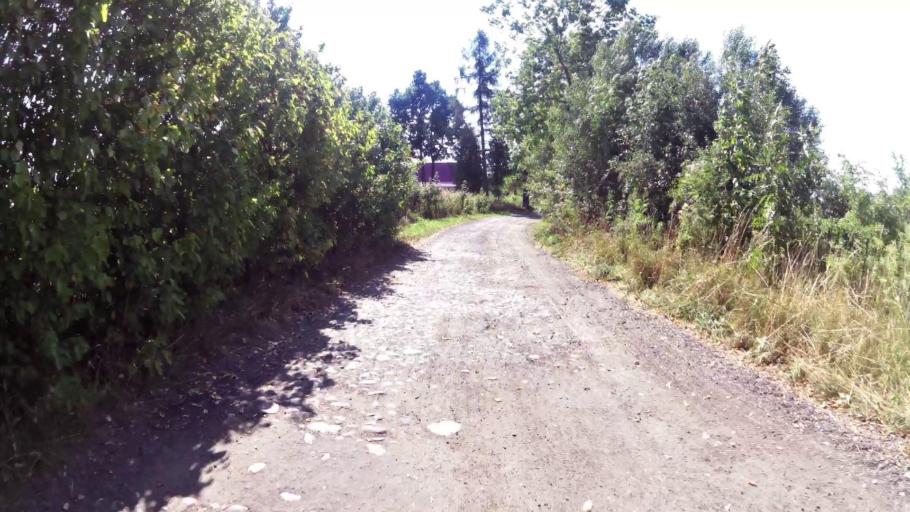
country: PL
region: West Pomeranian Voivodeship
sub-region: Powiat walecki
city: Walcz
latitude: 53.3342
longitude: 16.2980
